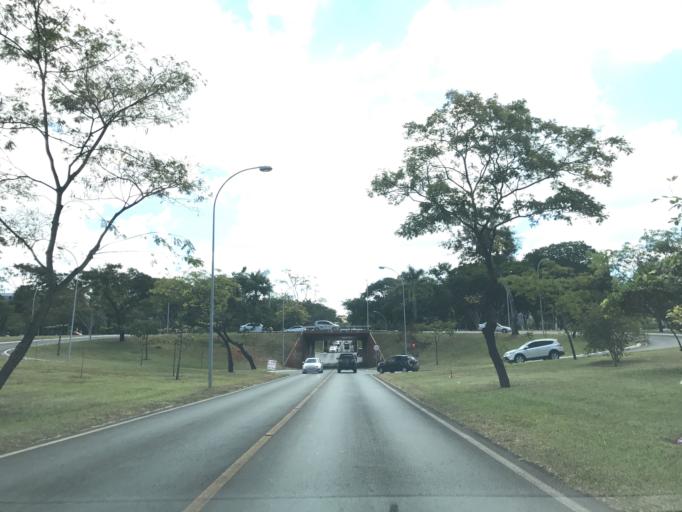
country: BR
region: Federal District
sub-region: Brasilia
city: Brasilia
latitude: -15.8341
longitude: -47.9217
